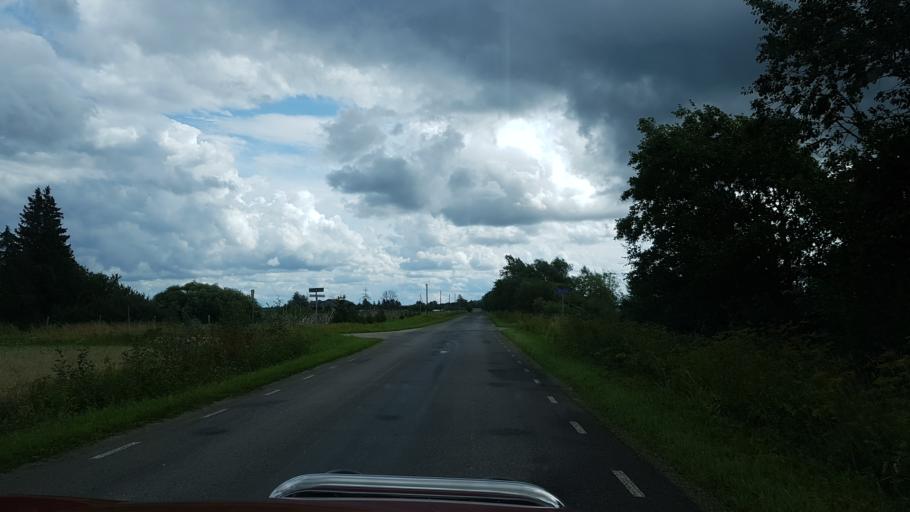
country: EE
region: Laeaene
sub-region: Lihula vald
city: Lihula
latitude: 58.7187
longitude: 23.9829
